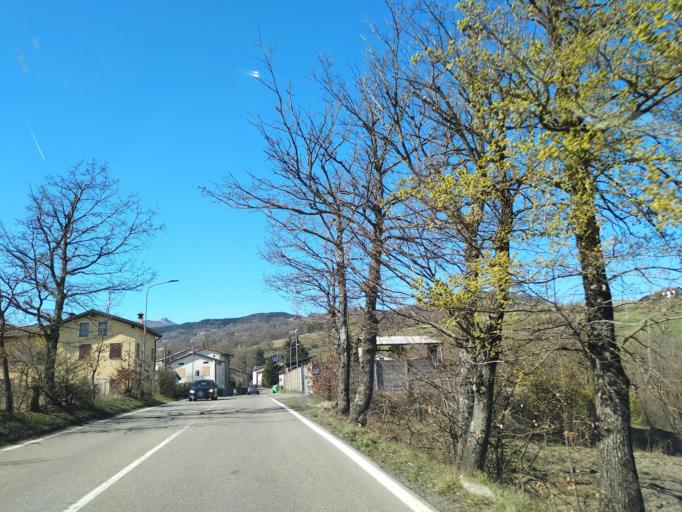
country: IT
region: Emilia-Romagna
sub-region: Provincia di Reggio Emilia
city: Castelnovo ne'Monti
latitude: 44.4206
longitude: 10.3769
